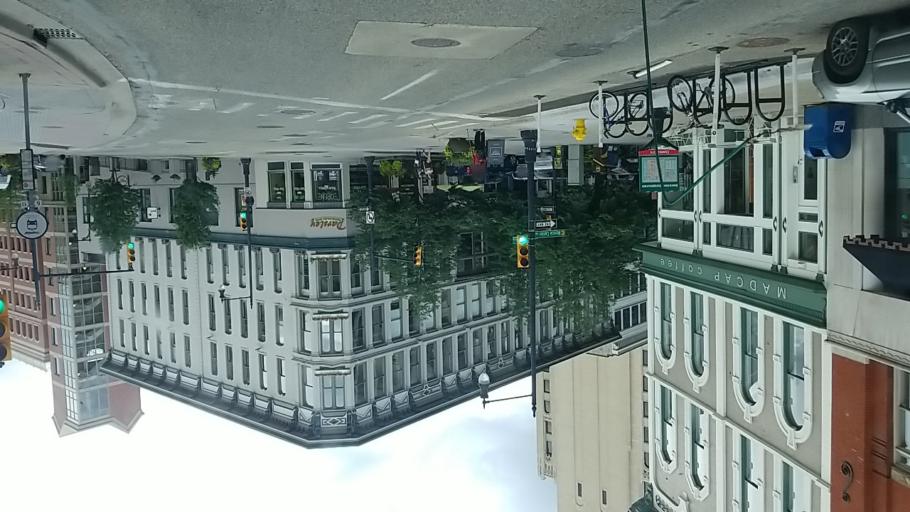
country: US
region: Michigan
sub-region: Kent County
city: Grand Rapids
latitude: 42.9654
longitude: -85.6702
